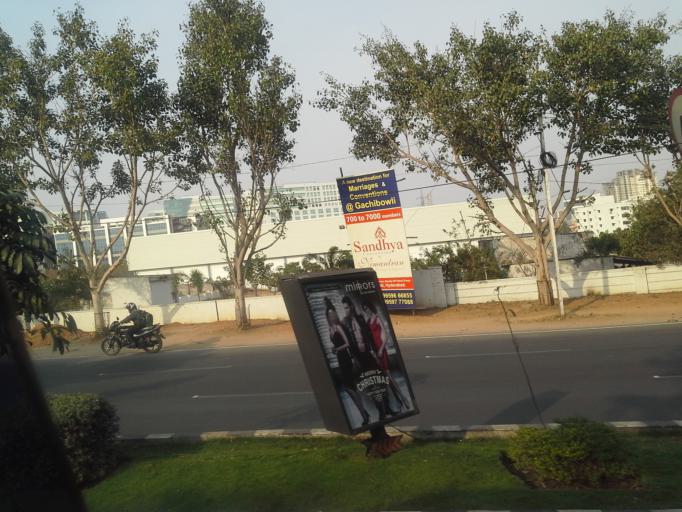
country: IN
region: Telangana
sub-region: Rangareddi
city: Kukatpalli
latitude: 17.4433
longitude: 78.3551
